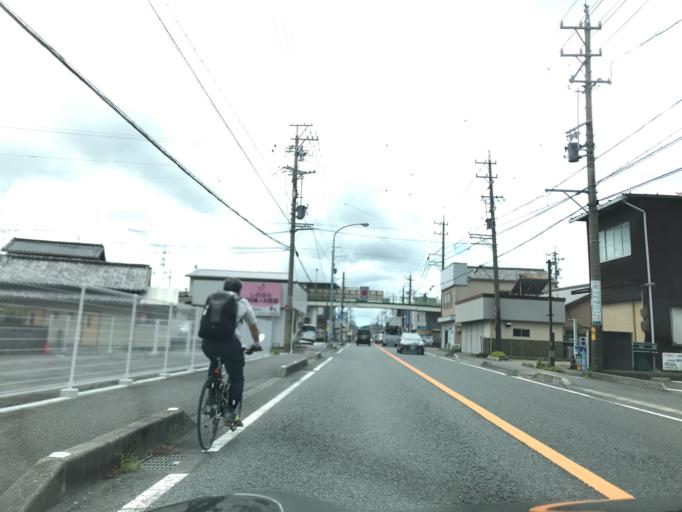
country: JP
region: Shizuoka
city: Shimada
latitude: 34.8435
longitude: 138.1815
